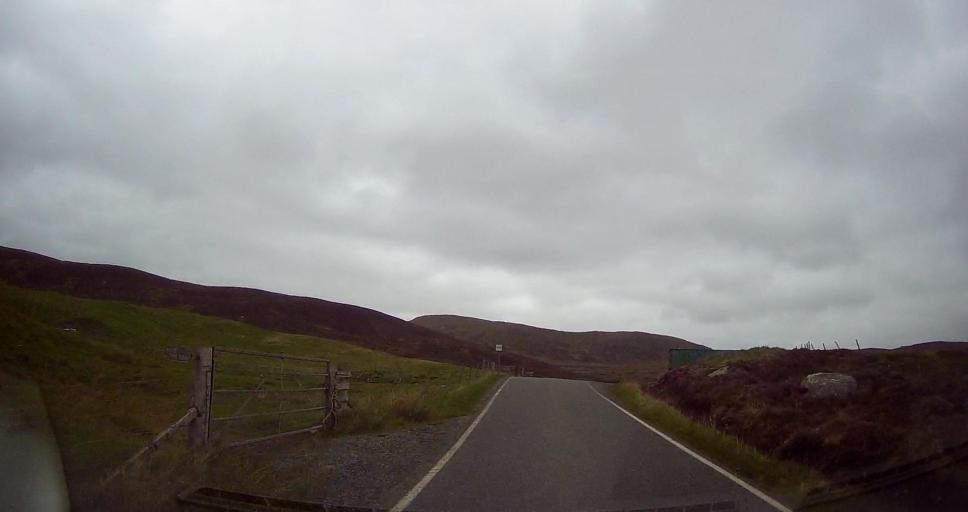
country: GB
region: Scotland
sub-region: Shetland Islands
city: Lerwick
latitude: 60.3014
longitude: -1.3446
